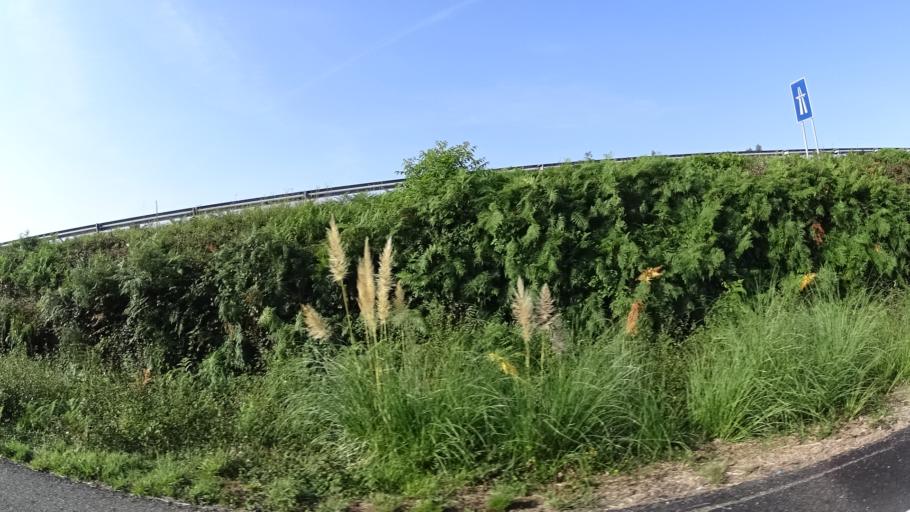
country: ES
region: Galicia
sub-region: Provincia da Coruna
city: Bergondo
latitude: 43.2784
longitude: -8.2644
